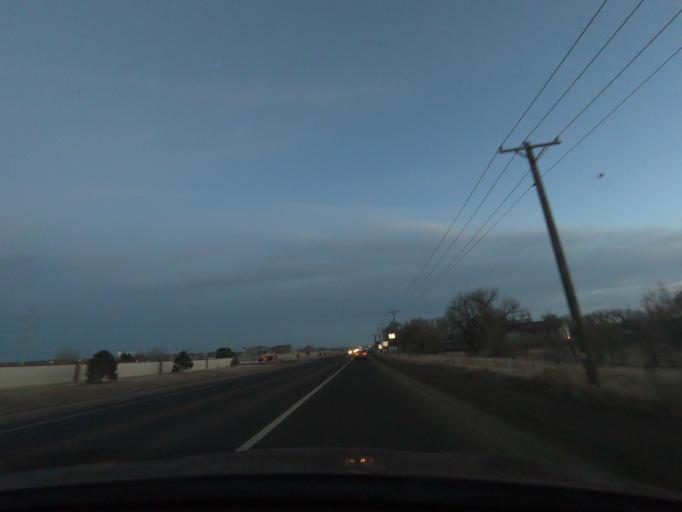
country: US
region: Colorado
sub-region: El Paso County
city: Stratmoor
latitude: 38.7747
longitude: -104.7681
